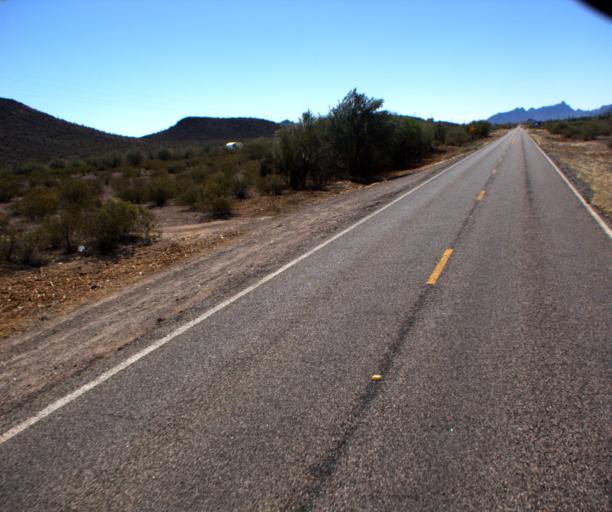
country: US
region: Arizona
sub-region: Pima County
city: Ajo
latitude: 32.2805
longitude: -112.7443
